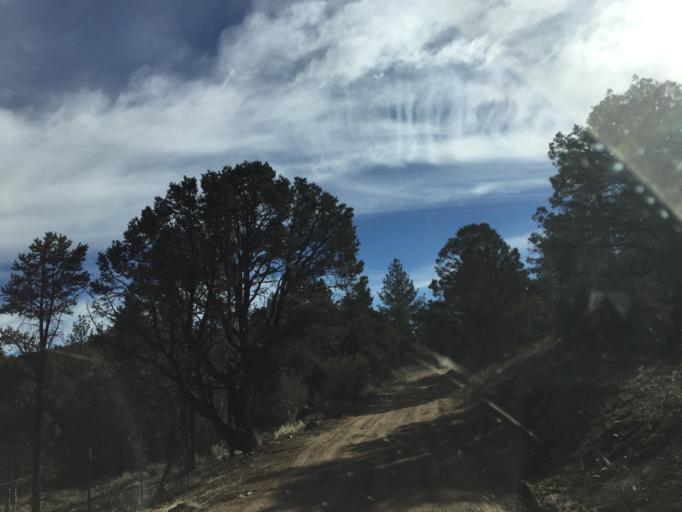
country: US
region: California
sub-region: San Bernardino County
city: Big Bear City
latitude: 34.2199
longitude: -116.7218
